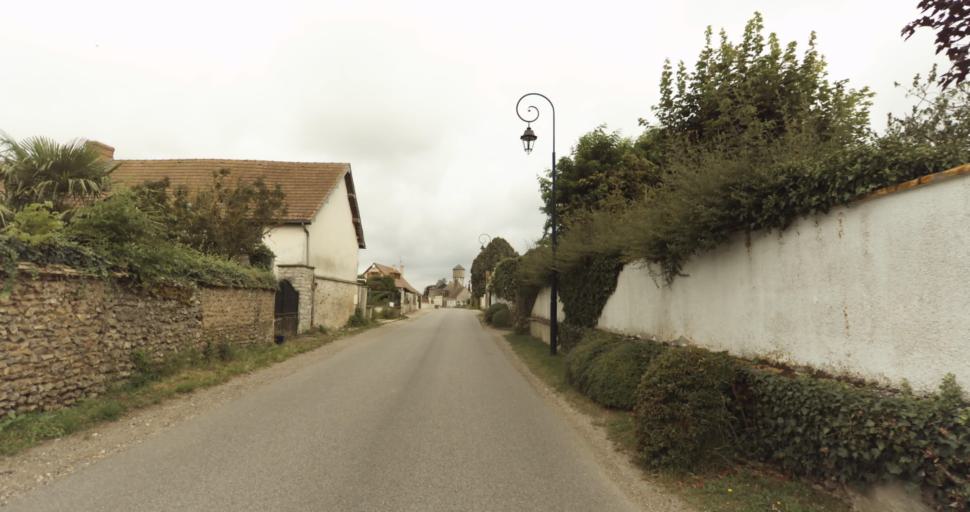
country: FR
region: Haute-Normandie
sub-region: Departement de l'Eure
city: La Couture-Boussey
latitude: 48.9319
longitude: 1.4002
